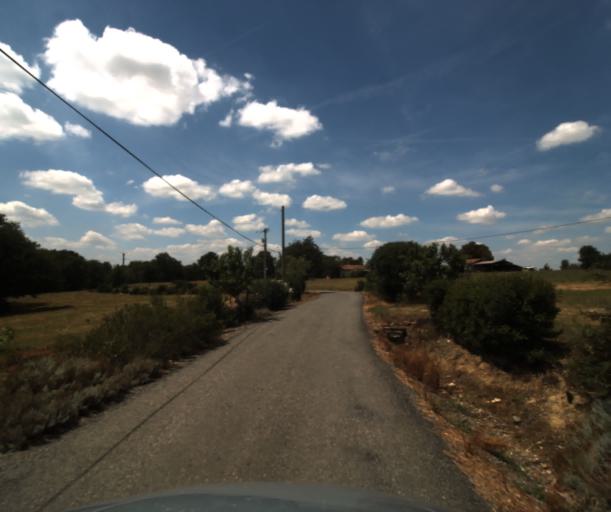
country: FR
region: Midi-Pyrenees
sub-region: Departement de la Haute-Garonne
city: Saint-Lys
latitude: 43.4863
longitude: 1.1846
